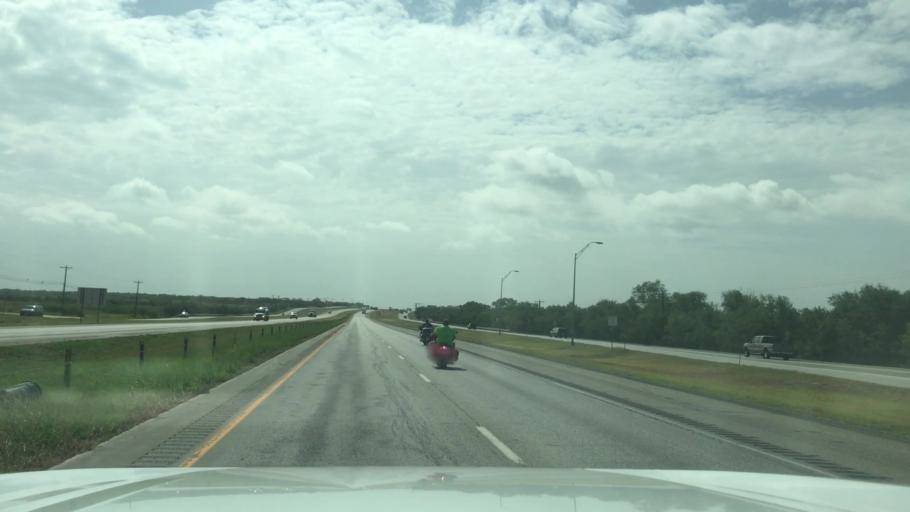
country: US
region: Texas
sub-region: Taylor County
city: Abilene
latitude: 32.4737
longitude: -99.6942
